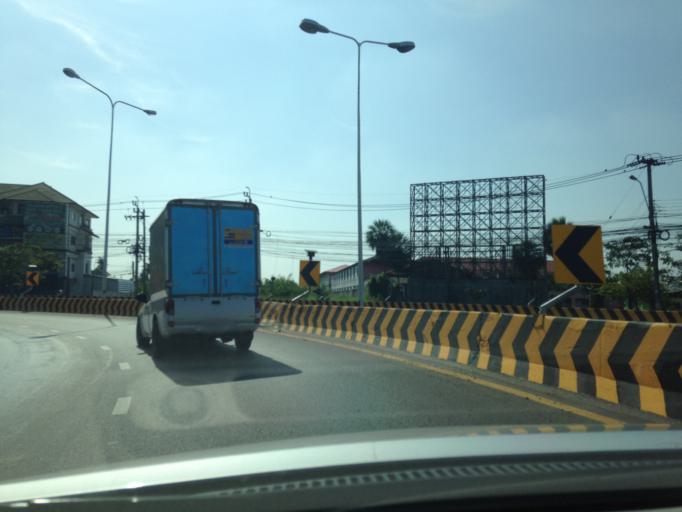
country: TH
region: Nonthaburi
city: Bang Yai
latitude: 13.8223
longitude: 100.4098
